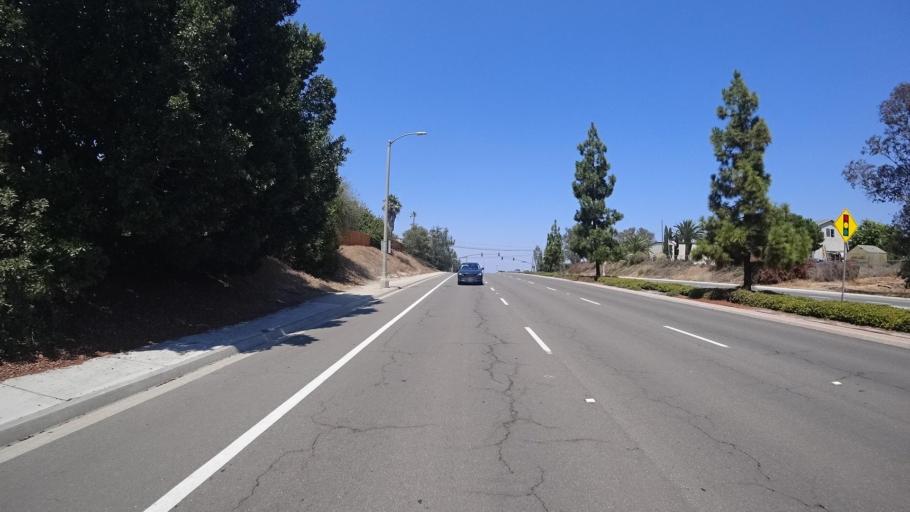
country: US
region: California
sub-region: San Diego County
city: Vista
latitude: 33.1767
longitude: -117.2537
